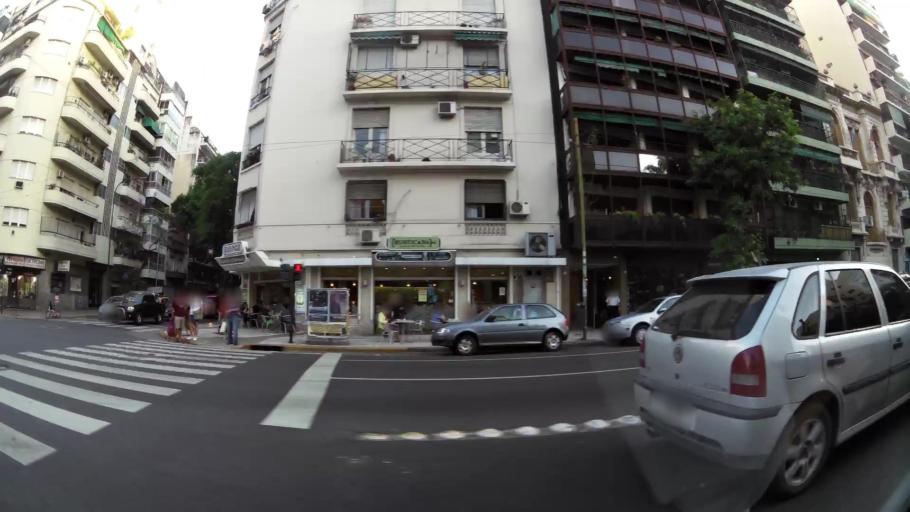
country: AR
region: Buenos Aires F.D.
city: Colegiales
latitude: -34.5874
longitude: -58.4180
